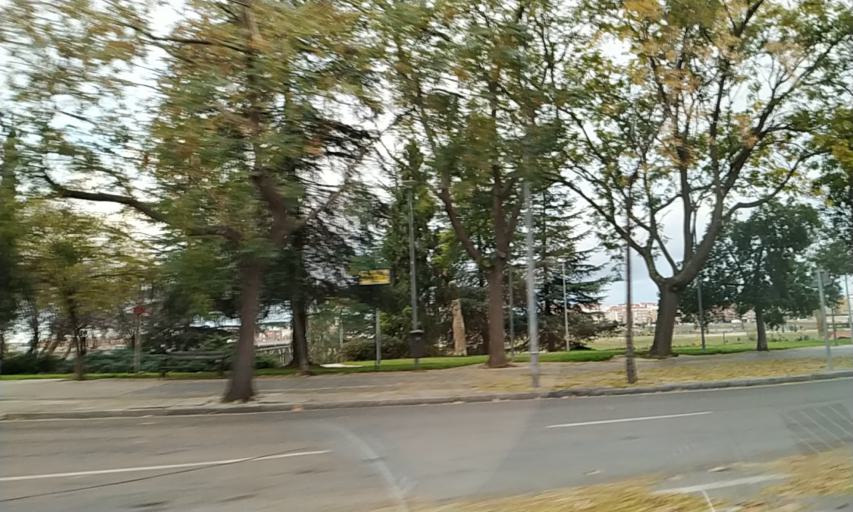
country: ES
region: Extremadura
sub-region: Provincia de Badajoz
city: Badajoz
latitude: 38.8783
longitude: -6.9801
